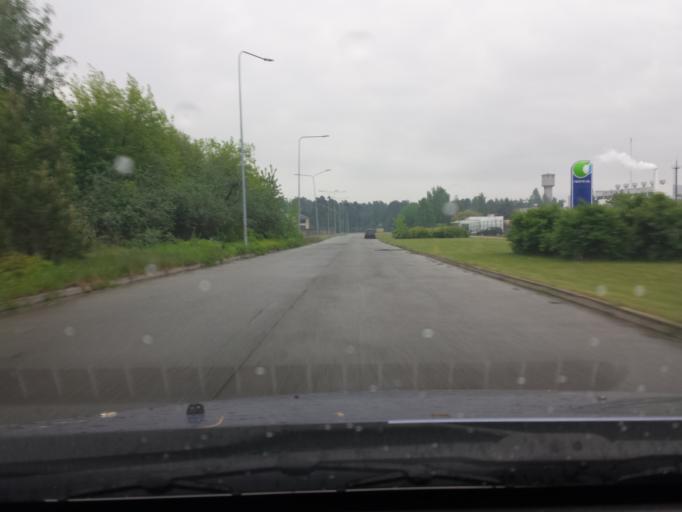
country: LV
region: Riga
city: Bolderaja
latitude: 57.0464
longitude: 24.0868
